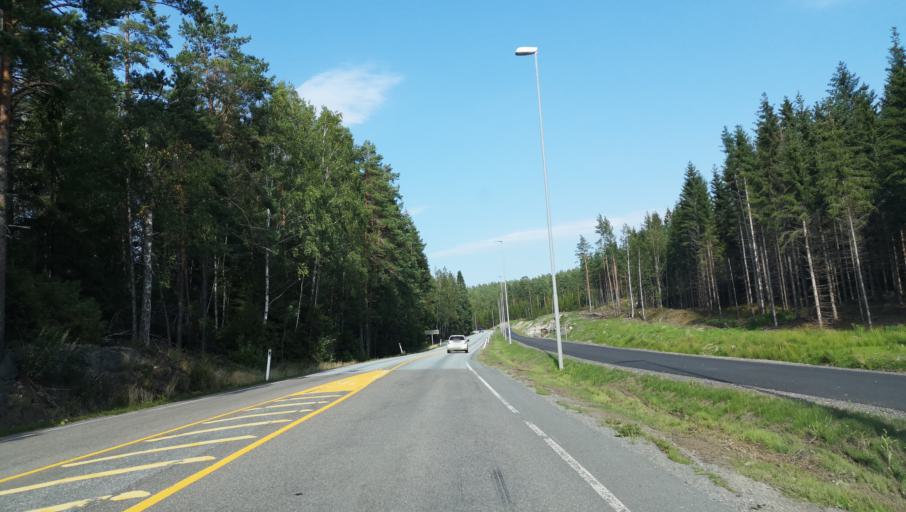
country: NO
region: Ostfold
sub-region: Valer
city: Kirkebygda
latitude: 59.4835
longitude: 10.7983
